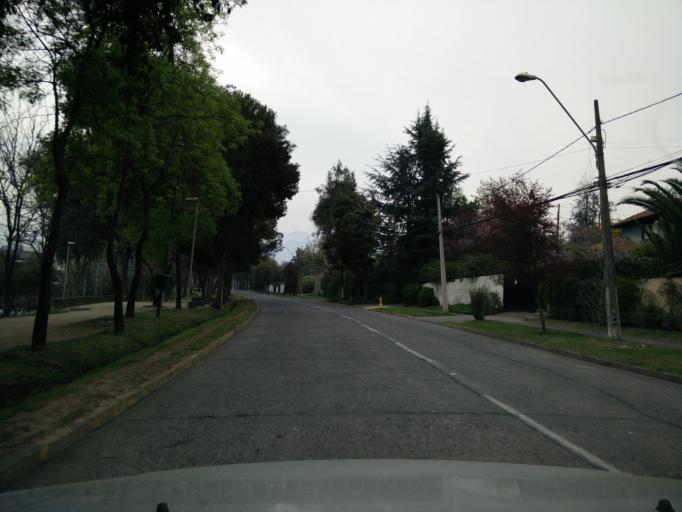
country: CL
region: Santiago Metropolitan
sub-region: Provincia de Santiago
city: Villa Presidente Frei, Nunoa, Santiago, Chile
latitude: -33.3911
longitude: -70.5288
